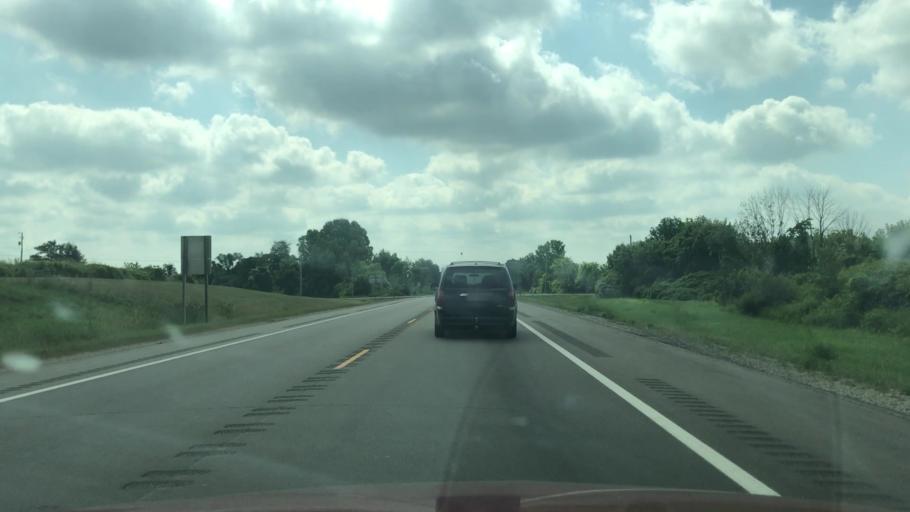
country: US
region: Michigan
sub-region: Kent County
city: Kent City
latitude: 43.2316
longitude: -85.7924
